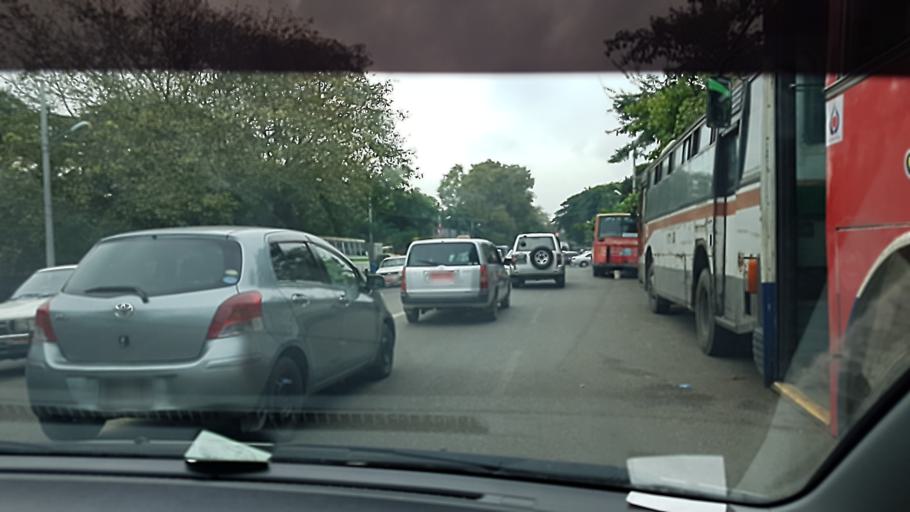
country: MM
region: Yangon
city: Yangon
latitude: 16.8164
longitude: 96.1260
